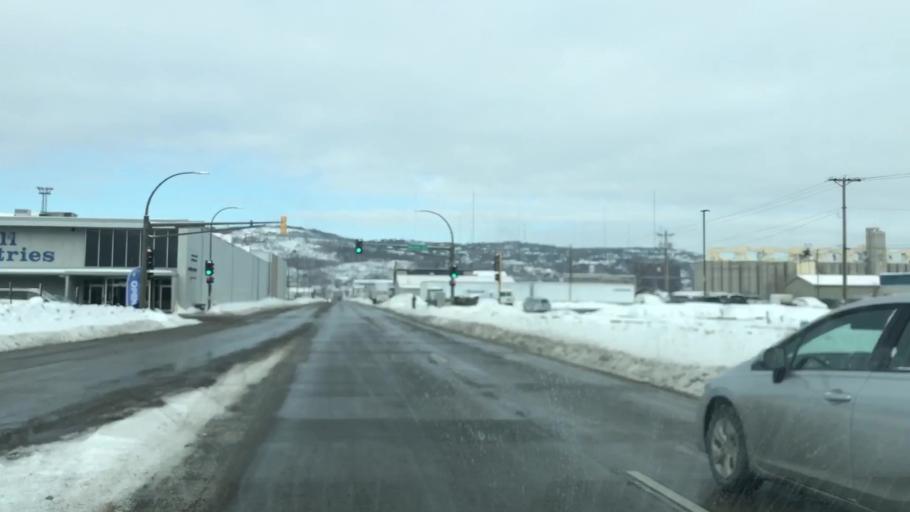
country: US
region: Minnesota
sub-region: Saint Louis County
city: Duluth
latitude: 46.7596
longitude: -92.1091
